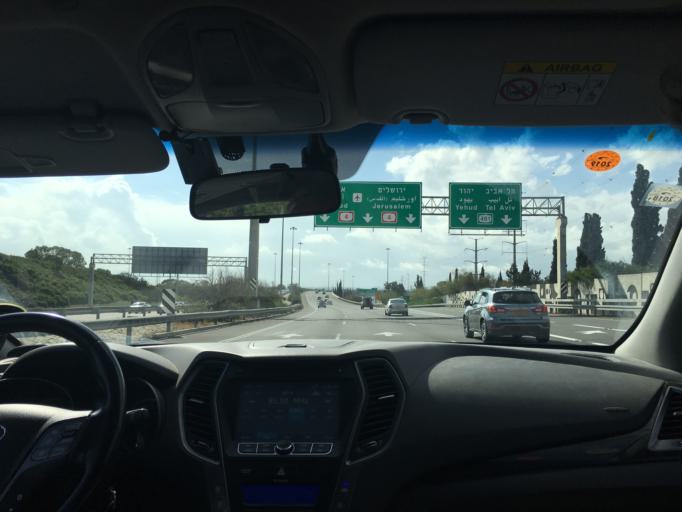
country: IL
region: Tel Aviv
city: Azor
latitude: 32.0426
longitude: 34.8295
